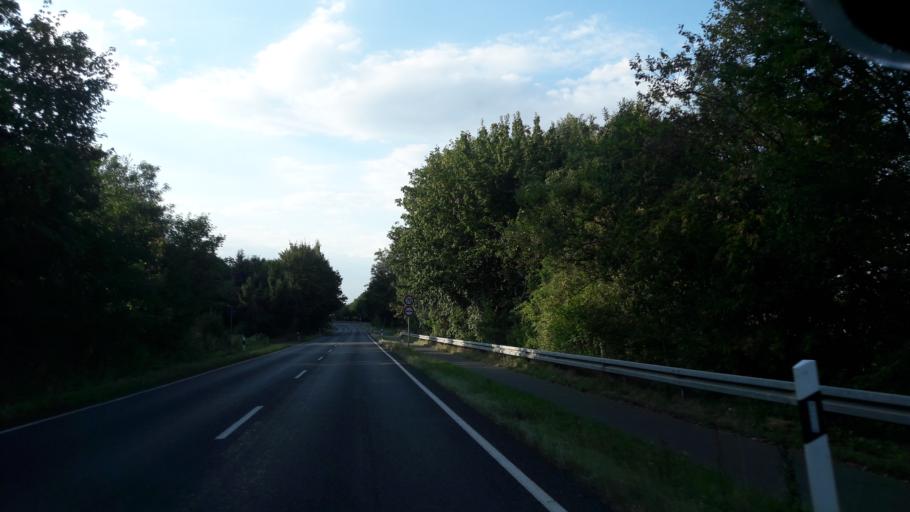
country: DE
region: Lower Saxony
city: Diekholzen
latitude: 52.1273
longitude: 9.8863
